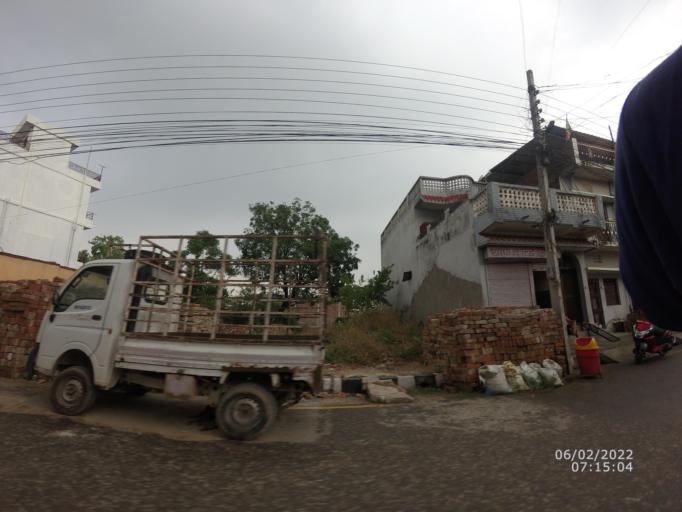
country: NP
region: Western Region
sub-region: Lumbini Zone
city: Bhairahawa
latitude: 27.4812
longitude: 83.4428
